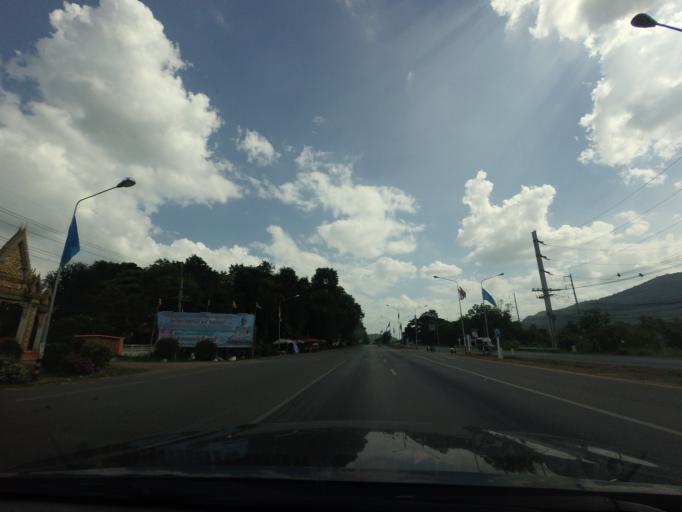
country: TH
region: Phetchabun
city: Wichian Buri
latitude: 15.6434
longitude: 101.0435
